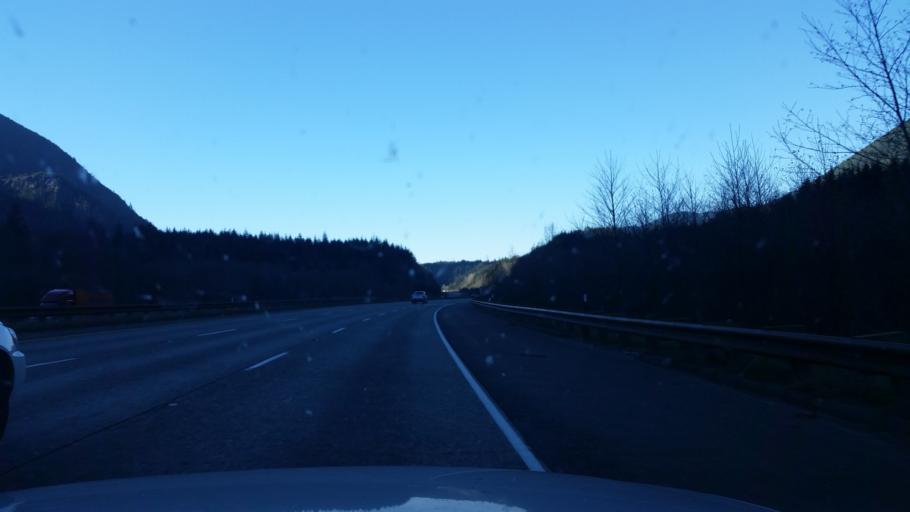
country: US
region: Washington
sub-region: King County
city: Tanner
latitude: 47.4309
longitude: -121.6357
